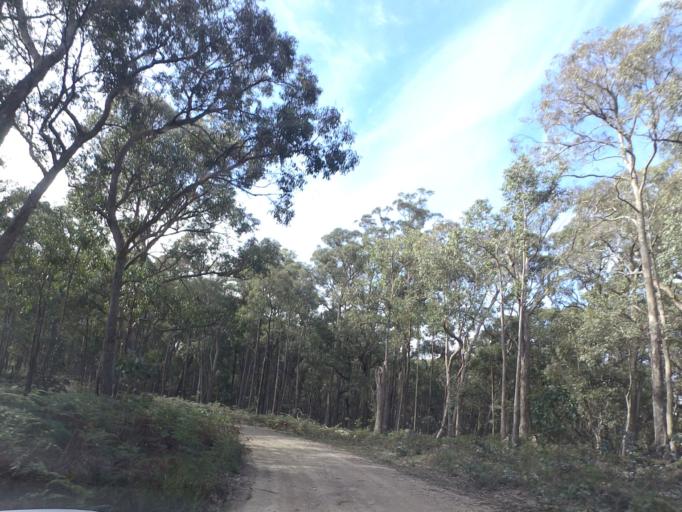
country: AU
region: Victoria
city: Brown Hill
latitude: -37.4922
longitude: 144.1899
